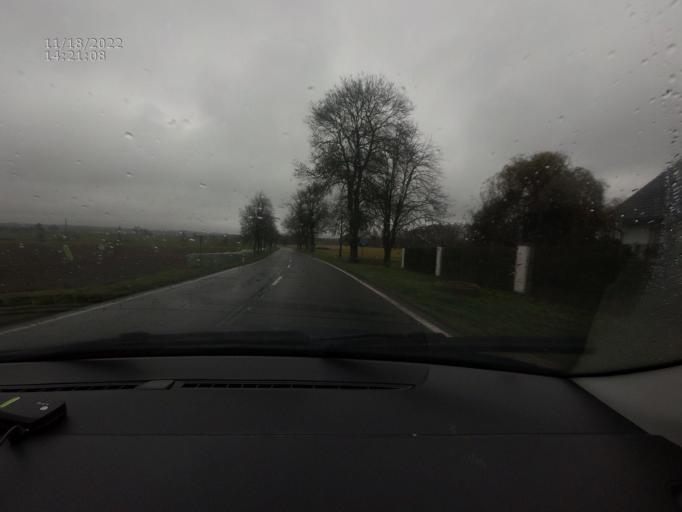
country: CZ
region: Jihocesky
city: Cimelice
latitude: 49.4418
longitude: 14.0859
